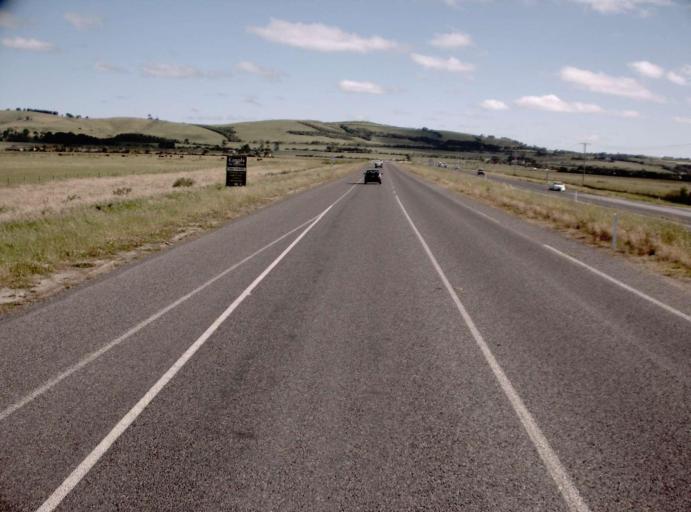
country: AU
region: Victoria
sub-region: Bass Coast
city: North Wonthaggi
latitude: -38.4928
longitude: 145.4635
